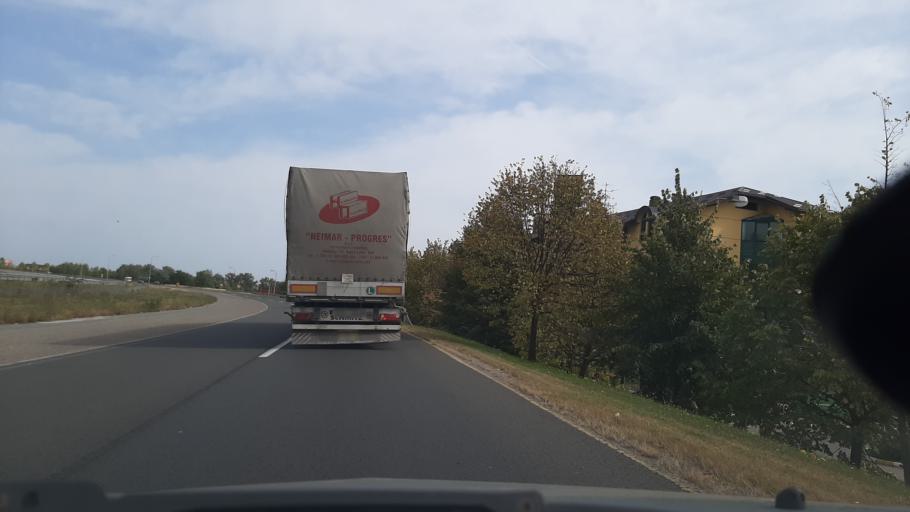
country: BA
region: Republika Srpska
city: Trn
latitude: 44.8711
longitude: 17.2779
